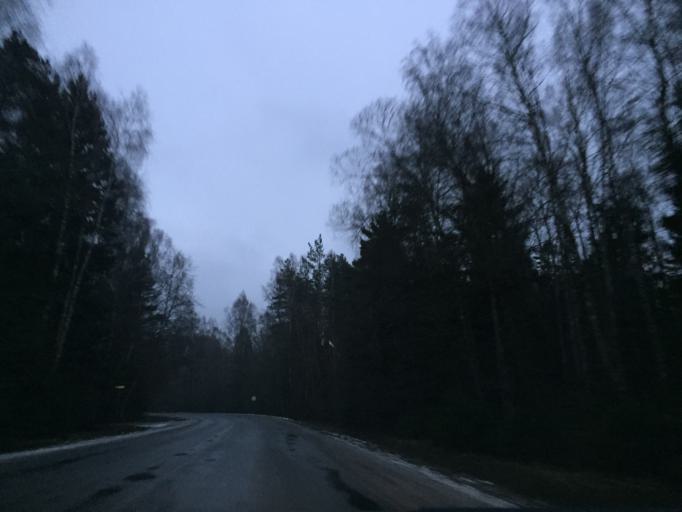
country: EE
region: Saare
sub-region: Kuressaare linn
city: Kuressaare
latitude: 58.5722
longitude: 22.6683
